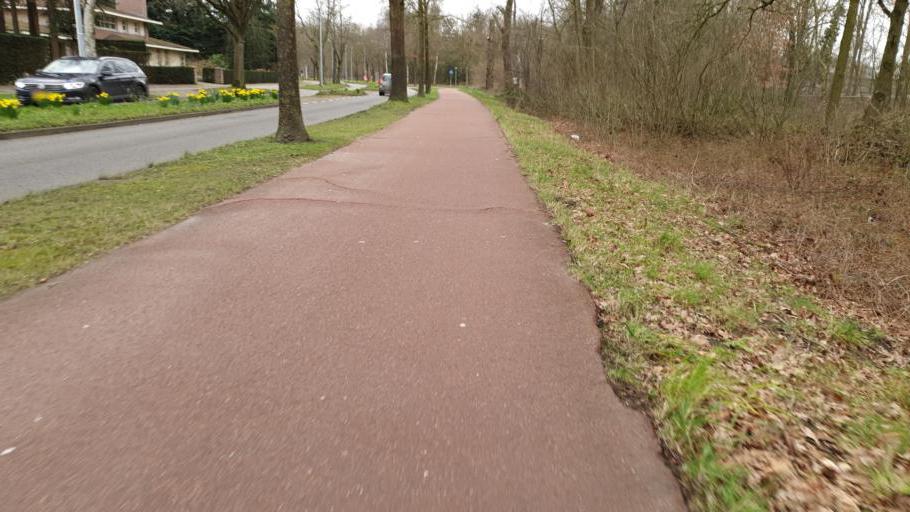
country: NL
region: North Brabant
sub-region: Gemeente Eindhoven
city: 't Hofke
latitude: 51.4572
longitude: 5.5060
